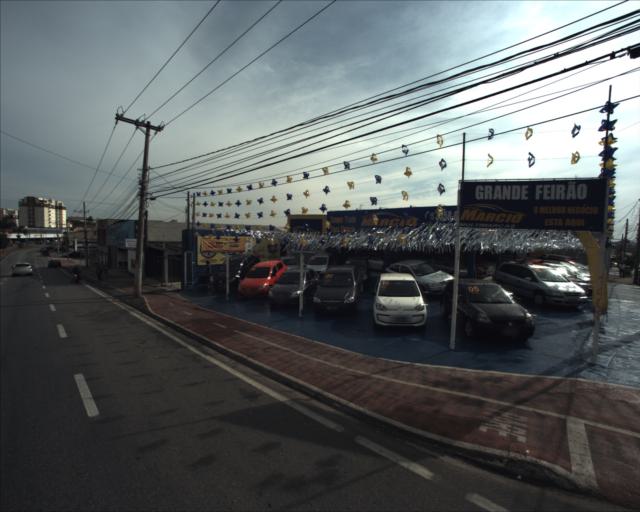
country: BR
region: Sao Paulo
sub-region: Sorocaba
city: Sorocaba
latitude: -23.4804
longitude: -47.4809
